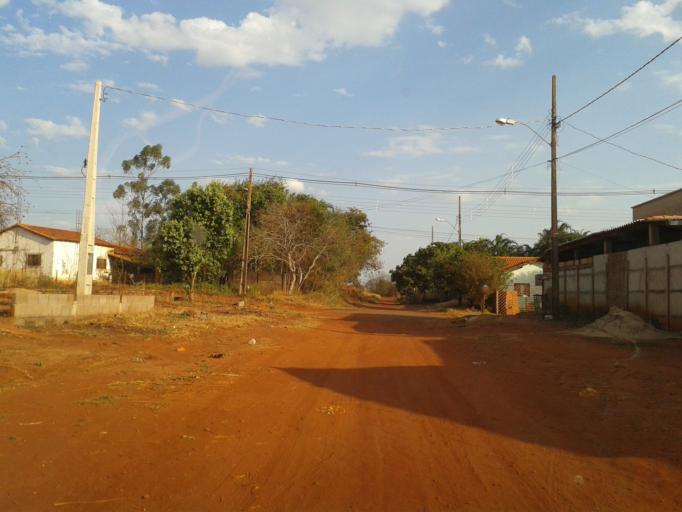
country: BR
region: Minas Gerais
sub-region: Ituiutaba
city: Ituiutaba
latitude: -18.9949
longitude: -49.4353
